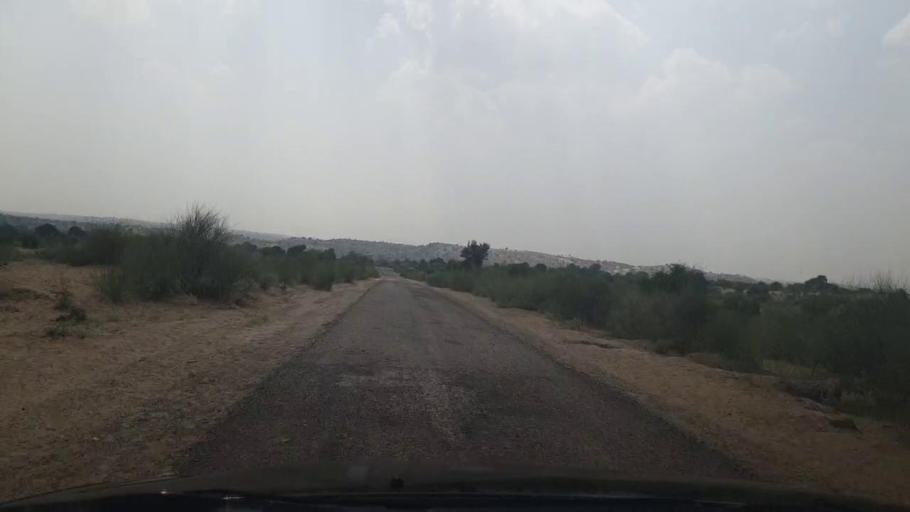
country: PK
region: Sindh
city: Islamkot
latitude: 24.9993
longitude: 70.4991
